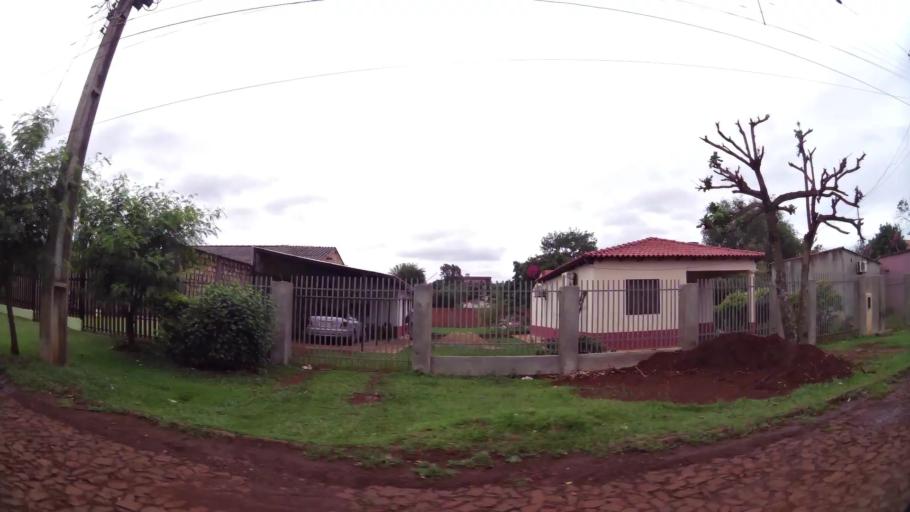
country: PY
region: Alto Parana
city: Ciudad del Este
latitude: -25.4000
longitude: -54.6382
